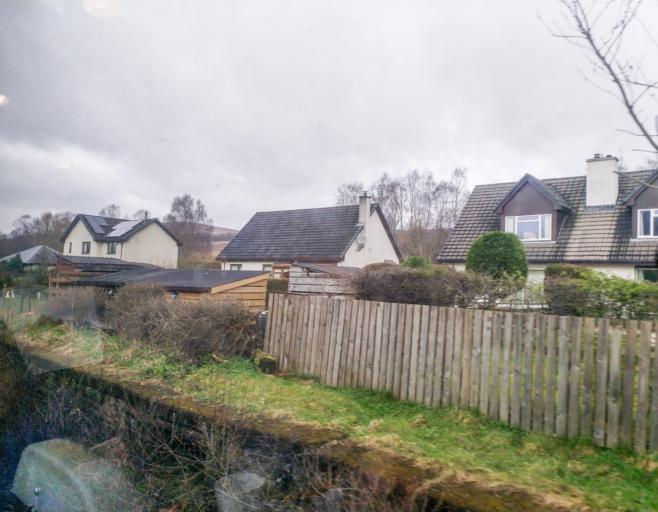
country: GB
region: Scotland
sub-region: Highland
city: Spean Bridge
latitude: 56.8886
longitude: -4.8380
